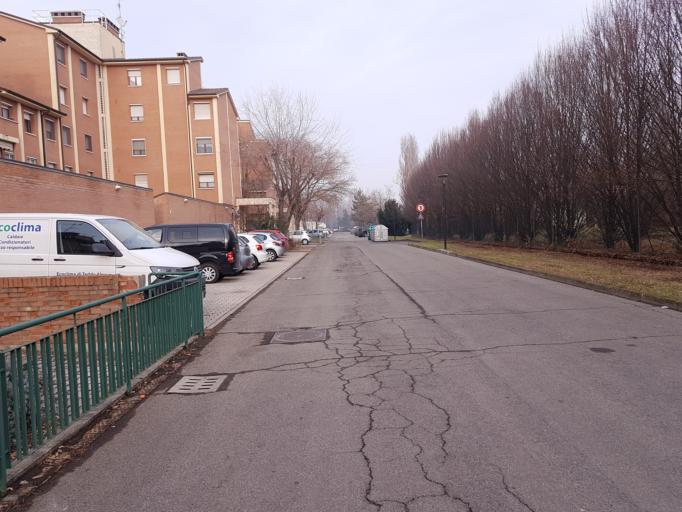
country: IT
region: Emilia-Romagna
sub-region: Provincia di Bologna
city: Quarto Inferiore
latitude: 44.5107
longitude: 11.3852
